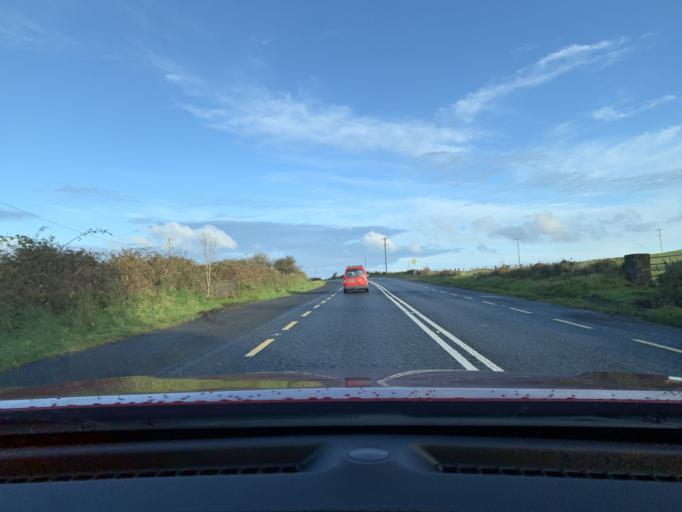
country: IE
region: Connaught
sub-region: Sligo
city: Sligo
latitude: 54.3637
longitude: -8.5270
